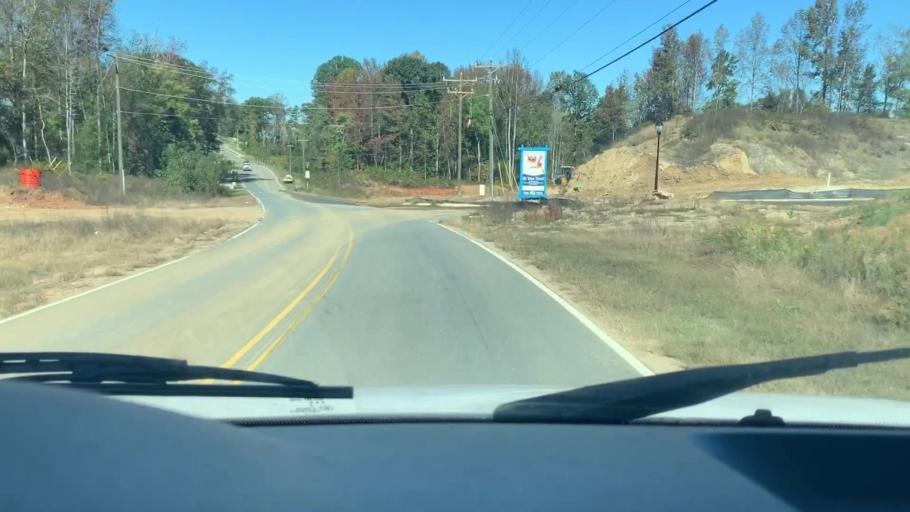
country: US
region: North Carolina
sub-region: Gaston County
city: Davidson
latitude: 35.4655
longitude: -80.8219
